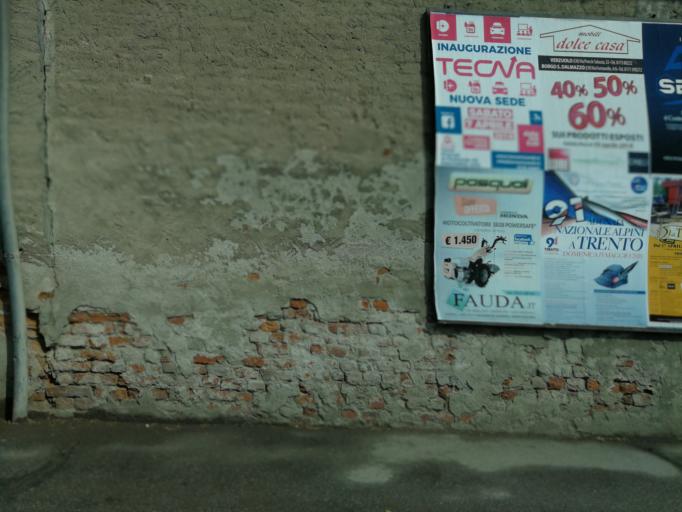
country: IT
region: Piedmont
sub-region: Provincia di Cuneo
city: Moretta
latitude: 44.7625
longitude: 7.5421
